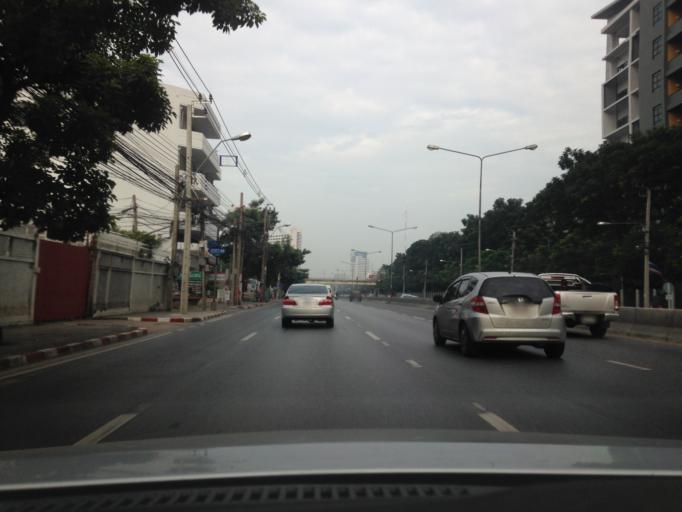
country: TH
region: Bangkok
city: Chatuchak
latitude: 13.8438
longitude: 100.5679
